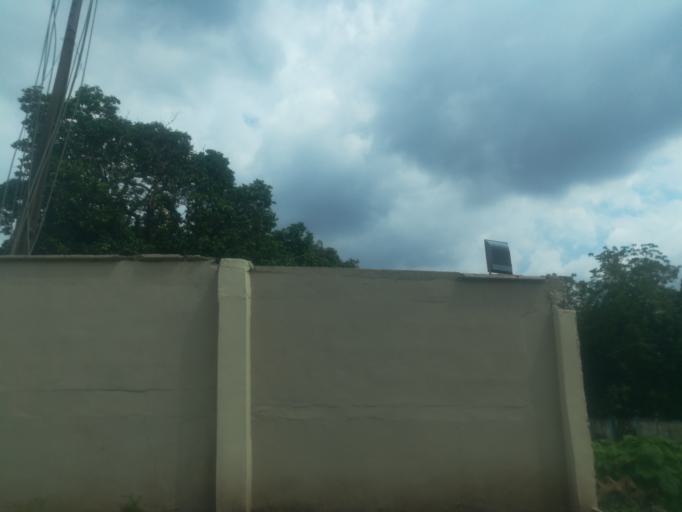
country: NG
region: Oyo
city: Ibadan
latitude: 7.3956
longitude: 3.8766
